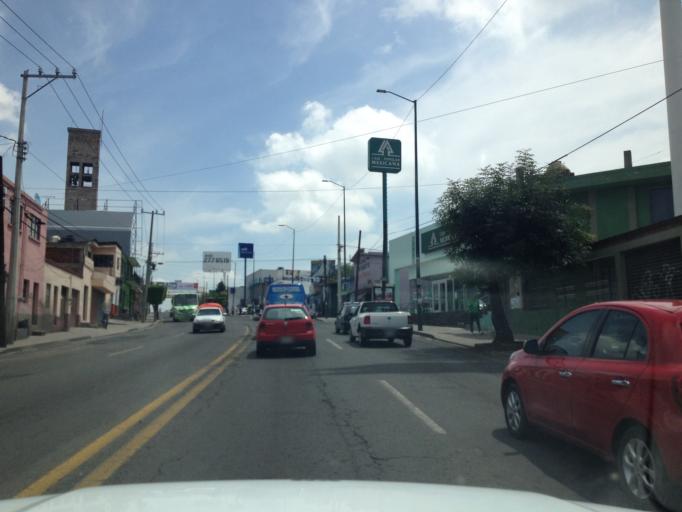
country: MX
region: Michoacan
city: Morelia
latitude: 19.7159
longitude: -101.1889
